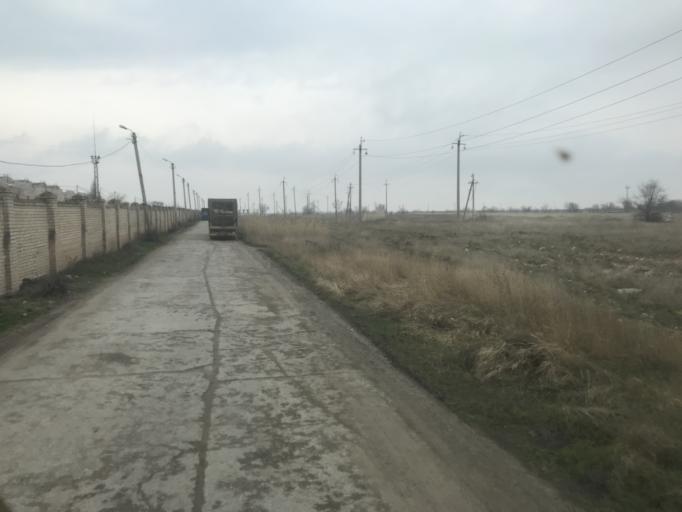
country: RU
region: Volgograd
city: Krasnoslobodsk
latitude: 48.5334
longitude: 44.5852
